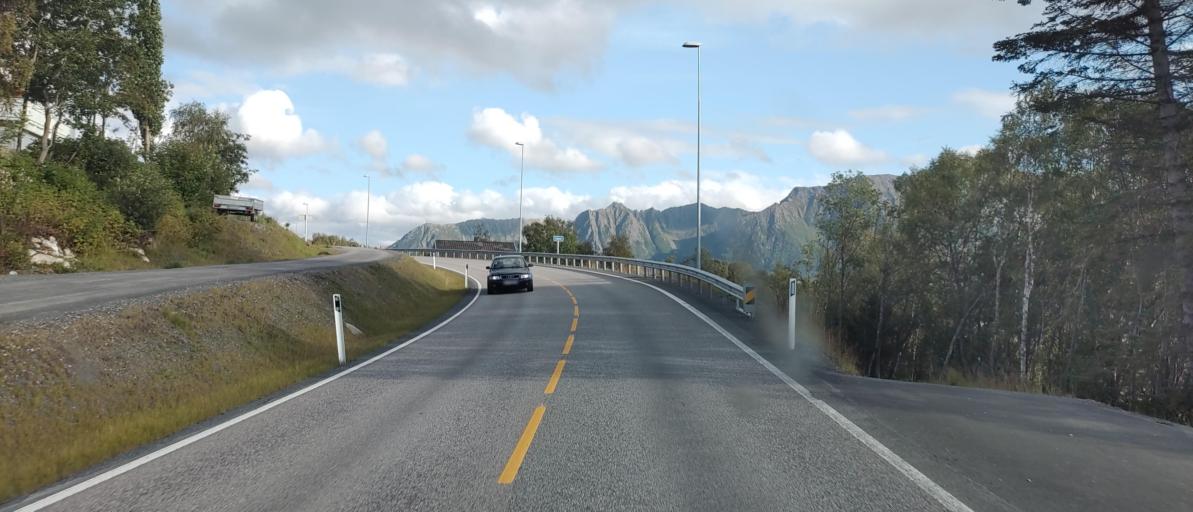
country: NO
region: Nordland
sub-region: Sortland
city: Sortland
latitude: 68.7520
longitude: 15.4748
